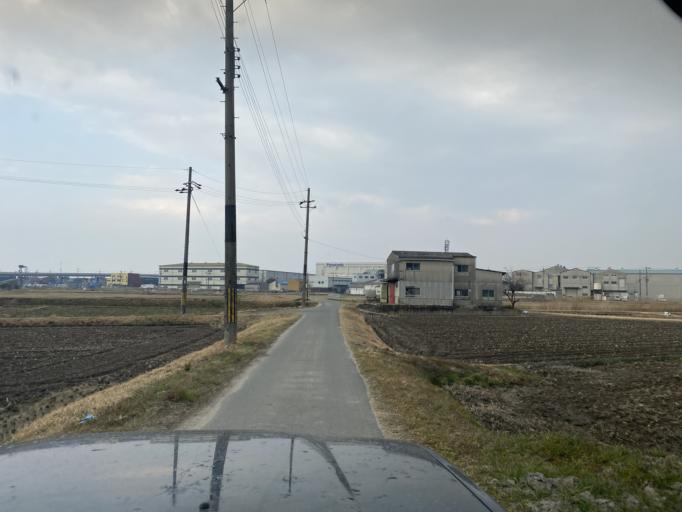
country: JP
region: Kyoto
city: Tanabe
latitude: 34.8410
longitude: 135.7473
